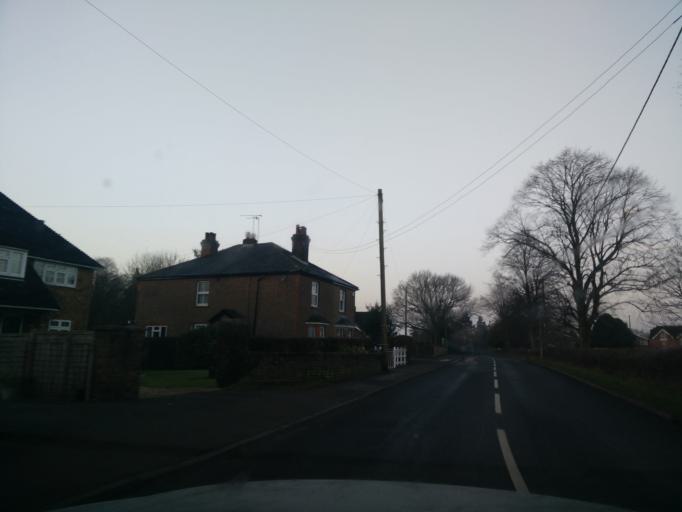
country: GB
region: England
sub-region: Buckinghamshire
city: Great Missenden
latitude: 51.6673
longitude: -0.6908
